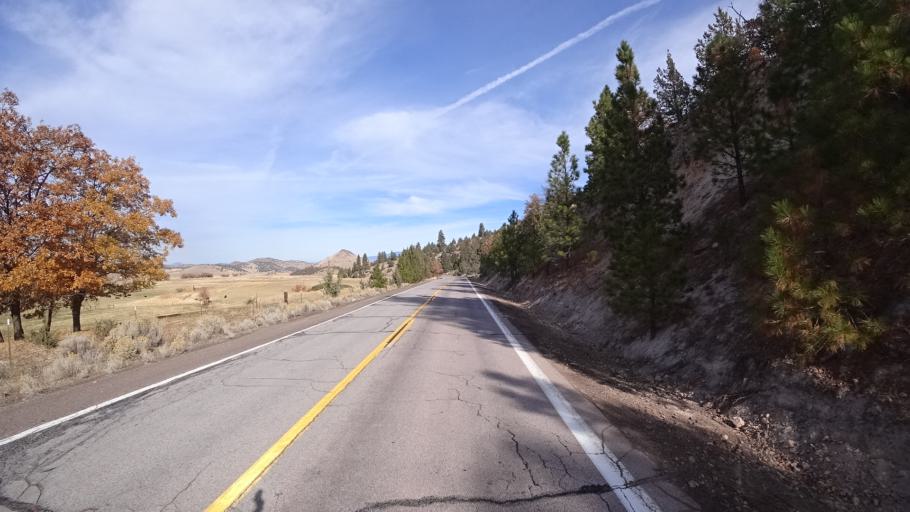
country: US
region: California
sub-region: Siskiyou County
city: Weed
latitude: 41.4755
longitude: -122.4126
